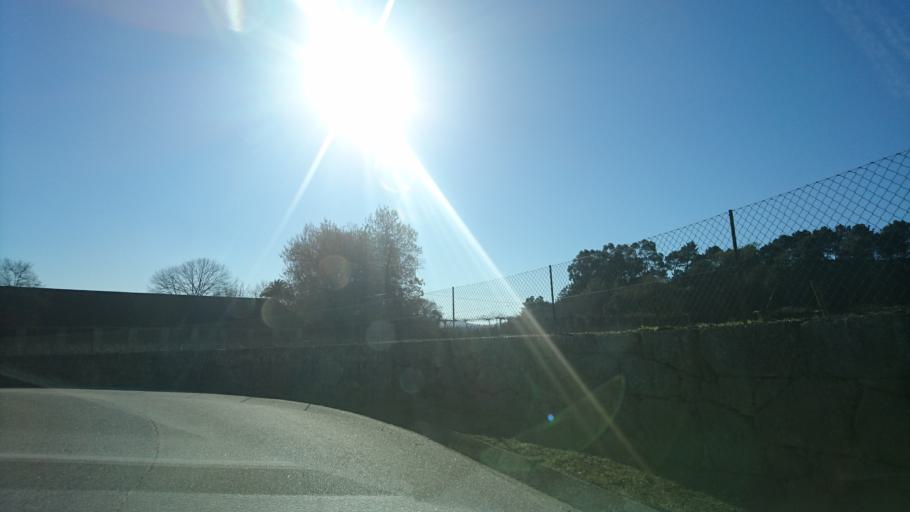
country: PT
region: Porto
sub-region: Paredes
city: Baltar
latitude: 41.1693
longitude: -8.3824
